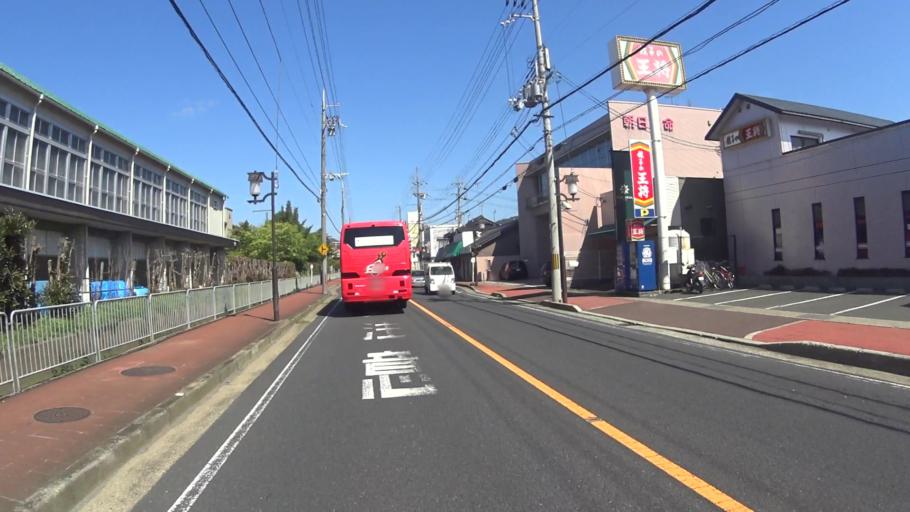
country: JP
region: Kyoto
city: Maizuru
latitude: 35.4378
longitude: 135.3284
